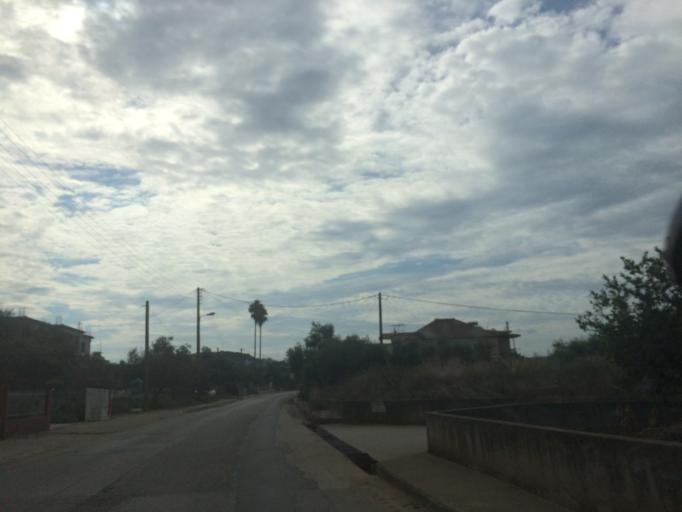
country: GR
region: Peloponnese
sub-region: Nomos Messinias
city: Pylos
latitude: 36.9612
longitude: 21.7001
